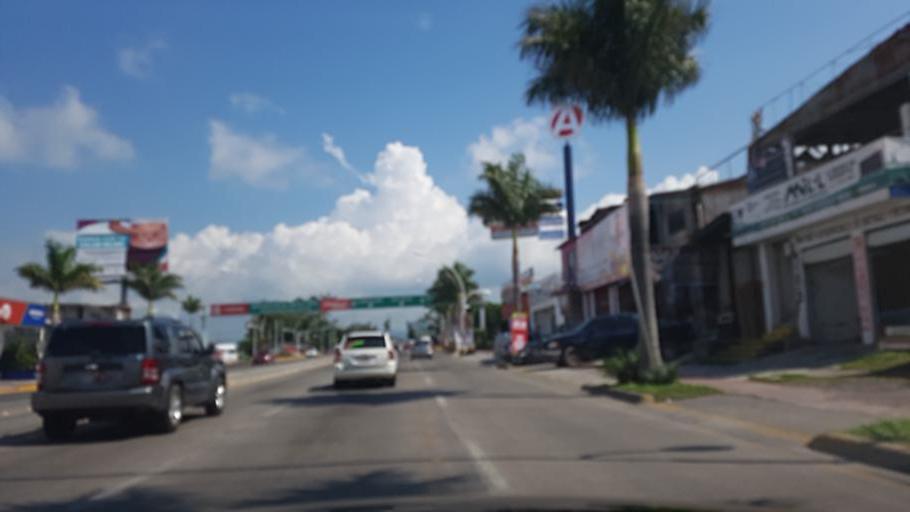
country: MX
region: Nayarit
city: Xalisco
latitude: 21.4740
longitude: -104.8900
